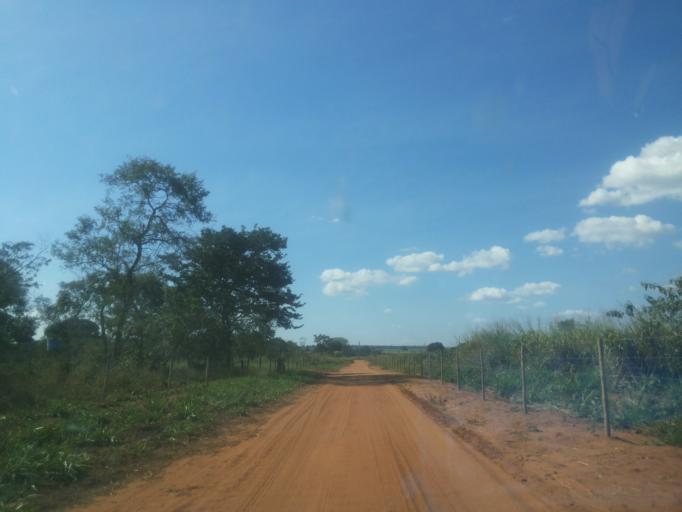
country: BR
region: Minas Gerais
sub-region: Santa Vitoria
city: Santa Vitoria
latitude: -18.9915
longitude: -50.3734
